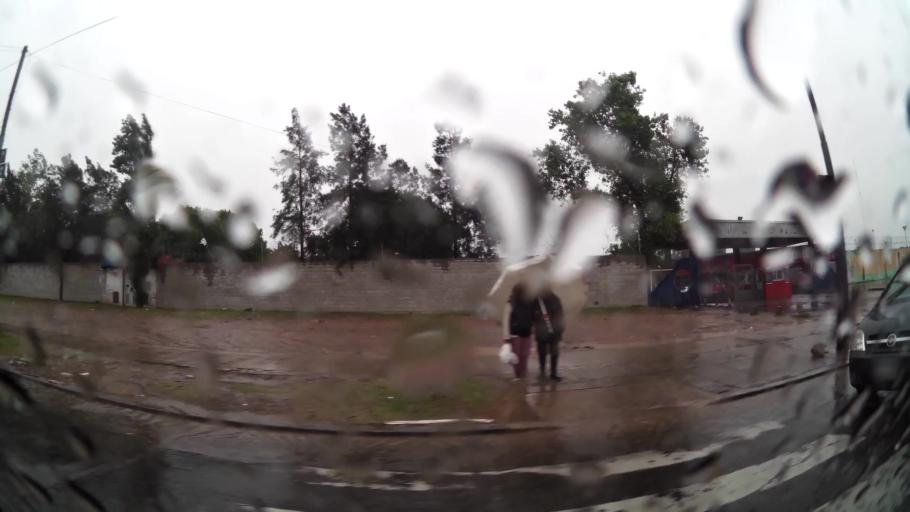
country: AR
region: Buenos Aires F.D.
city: Villa Lugano
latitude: -34.6529
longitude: -58.4345
